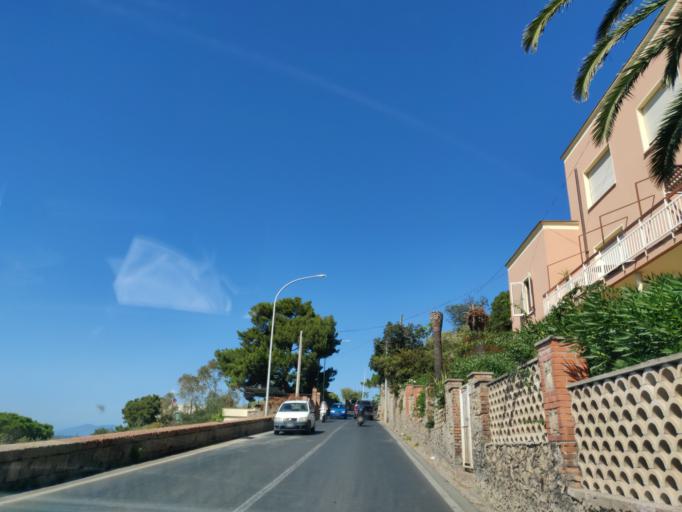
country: IT
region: Tuscany
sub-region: Provincia di Grosseto
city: Monte Argentario
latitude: 42.4358
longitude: 11.1260
